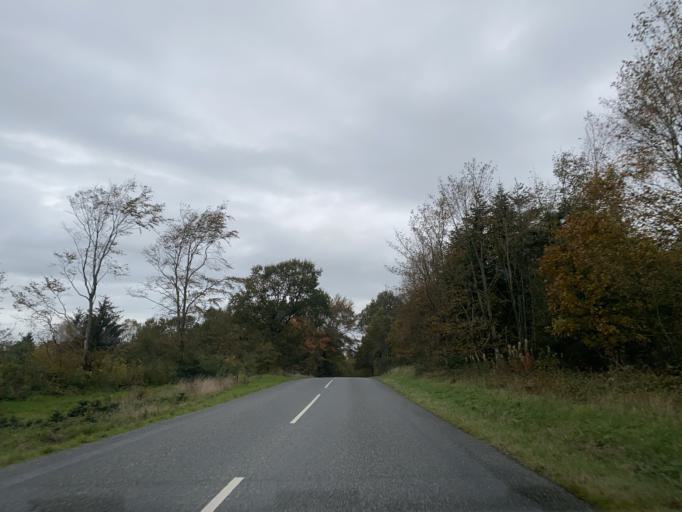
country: DK
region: Central Jutland
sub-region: Skanderborg Kommune
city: Ry
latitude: 56.1969
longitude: 9.7593
